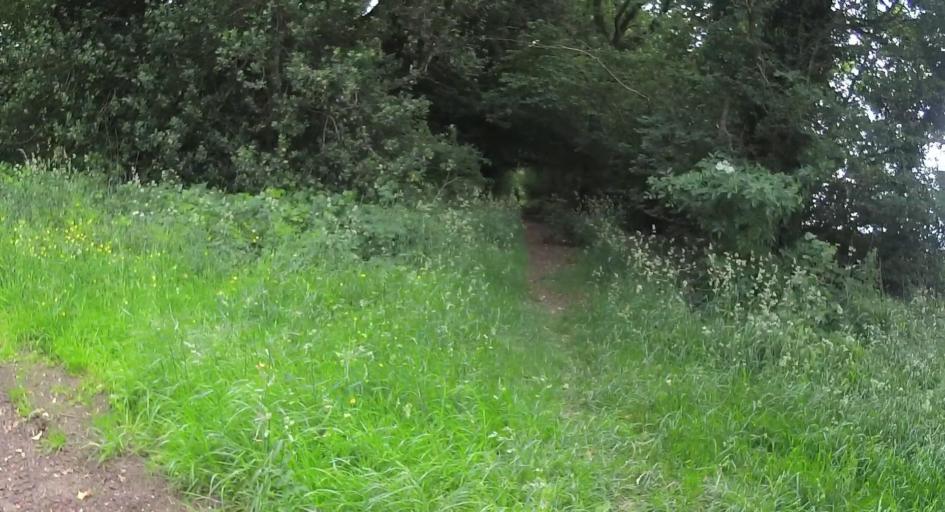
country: GB
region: England
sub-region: Hampshire
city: Overton
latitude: 51.1690
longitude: -1.1658
